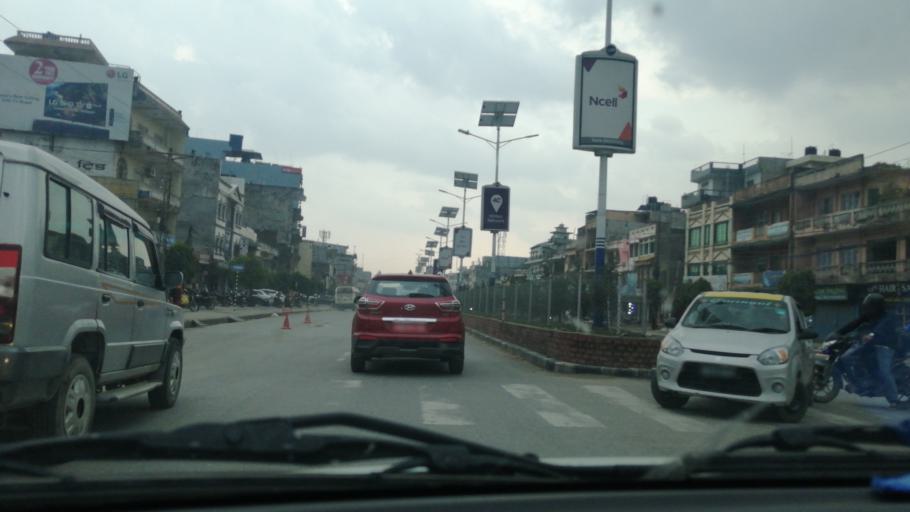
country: NP
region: Western Region
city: Butwal
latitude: 27.7039
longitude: 83.4668
